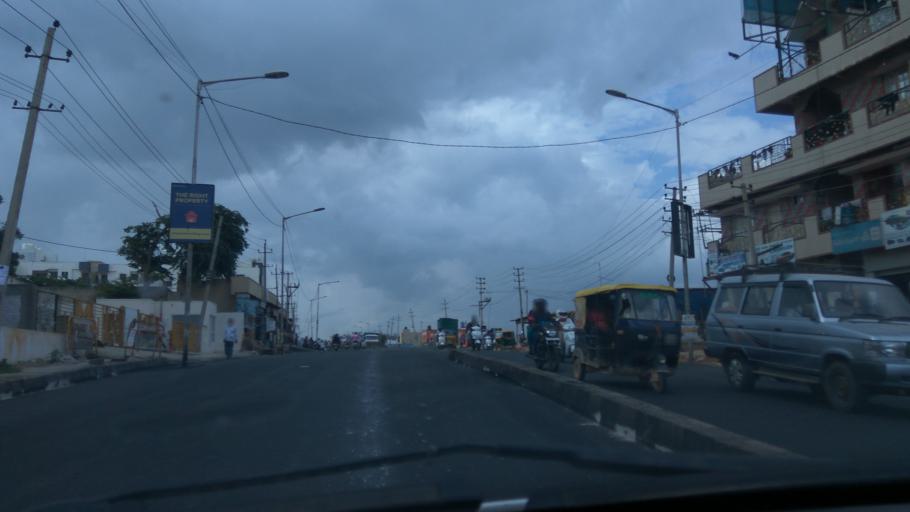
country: IN
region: Karnataka
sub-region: Bangalore Urban
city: Yelahanka
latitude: 13.0608
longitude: 77.6330
